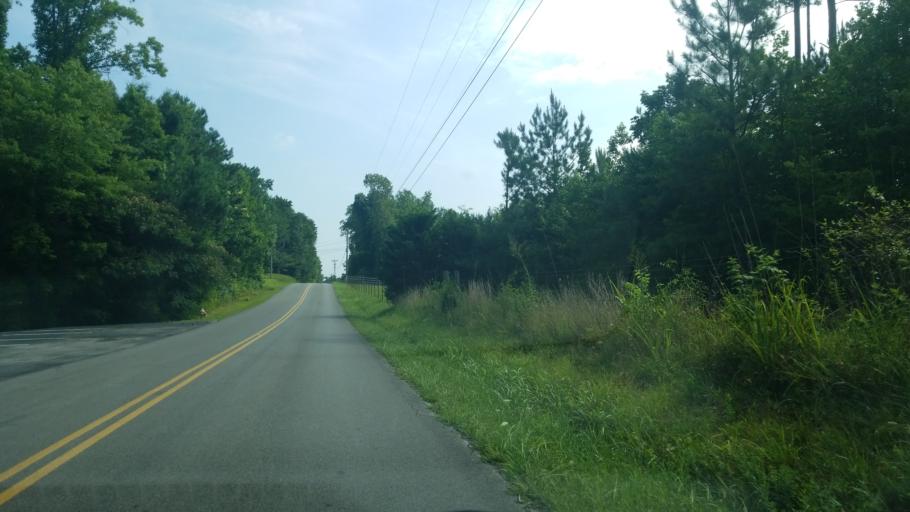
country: US
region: Tennessee
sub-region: Hamilton County
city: Apison
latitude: 35.0734
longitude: -84.9770
